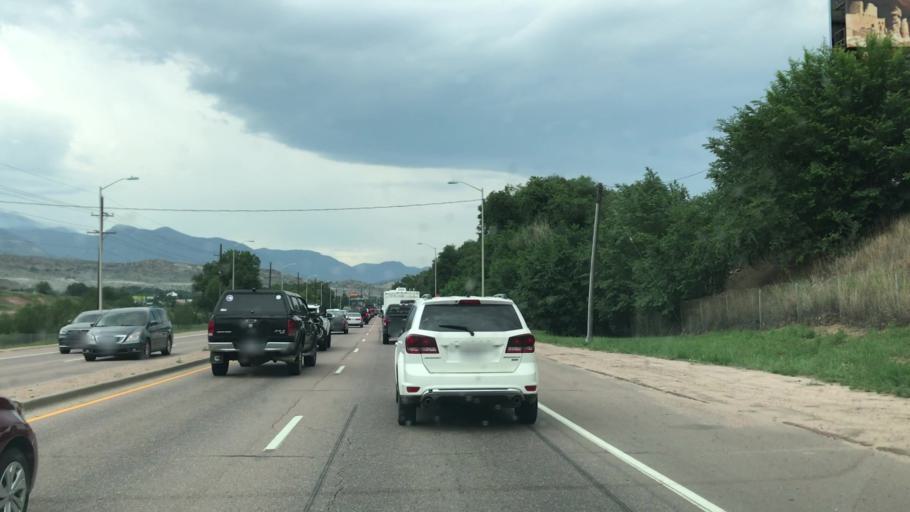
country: US
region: Colorado
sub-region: El Paso County
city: Colorado Springs
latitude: 38.8371
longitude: -104.8518
